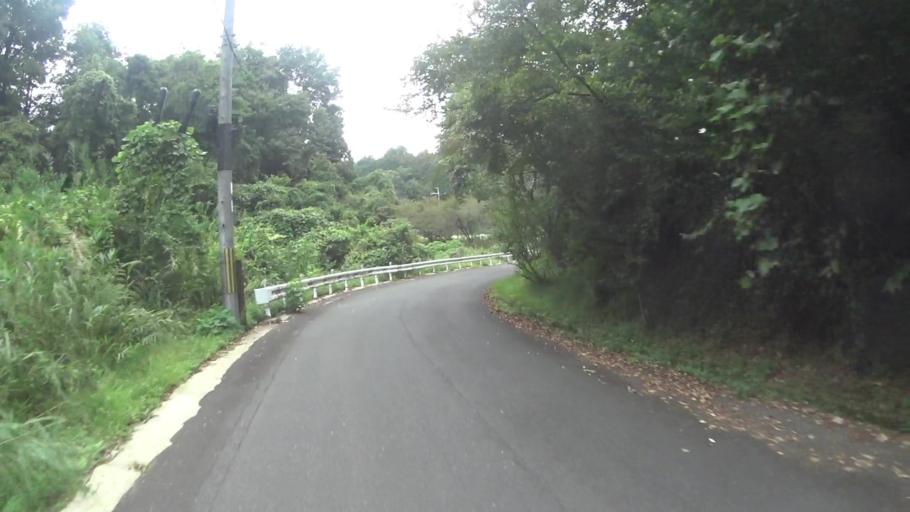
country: JP
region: Kyoto
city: Tanabe
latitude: 34.8116
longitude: 135.8583
